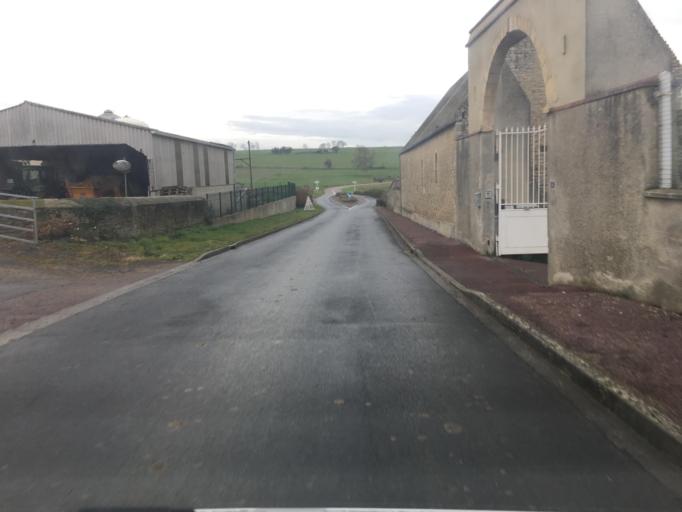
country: FR
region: Lower Normandy
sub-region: Departement du Calvados
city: Ver-sur-Mer
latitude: 49.3311
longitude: -0.6054
